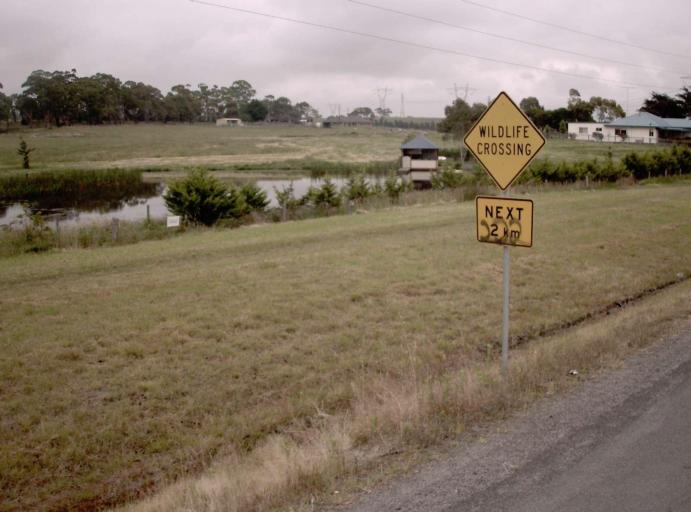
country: AU
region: Victoria
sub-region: Latrobe
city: Traralgon
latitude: -38.2553
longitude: 146.4885
